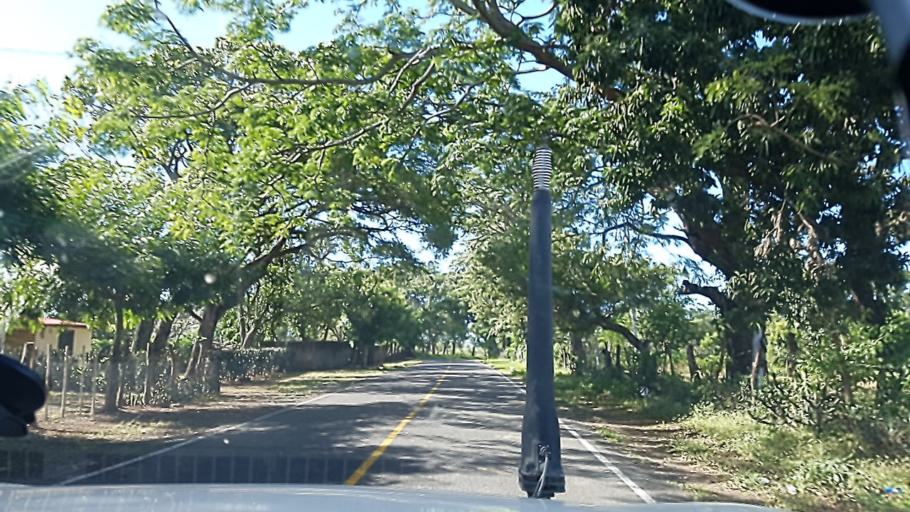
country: NI
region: Carazo
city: Santa Teresa
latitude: 11.7521
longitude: -86.1702
